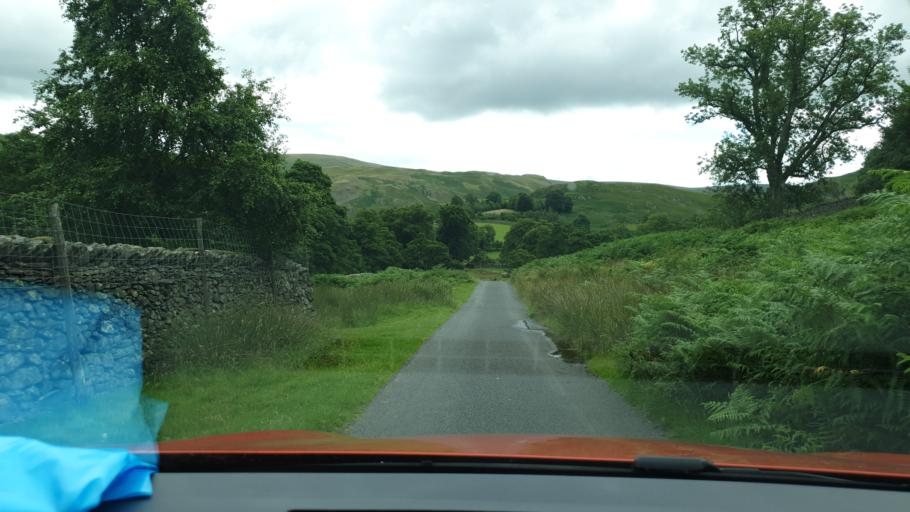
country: GB
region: England
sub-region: Cumbria
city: Ambleside
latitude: 54.5666
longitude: -2.8912
